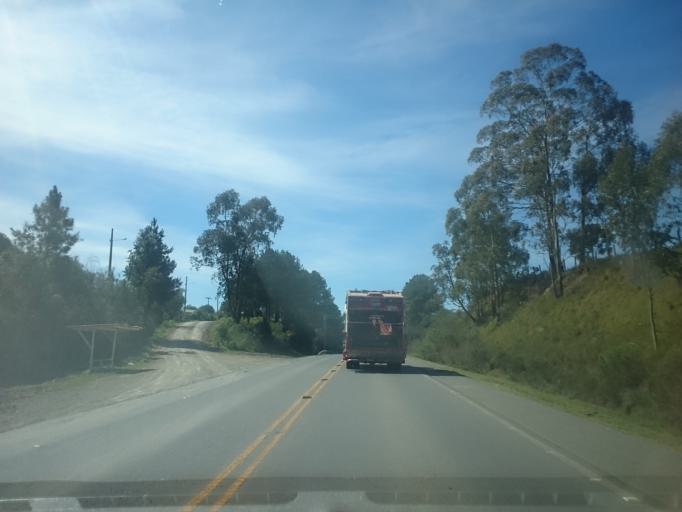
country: BR
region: Santa Catarina
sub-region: Lages
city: Lages
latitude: -27.7731
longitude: -50.1986
